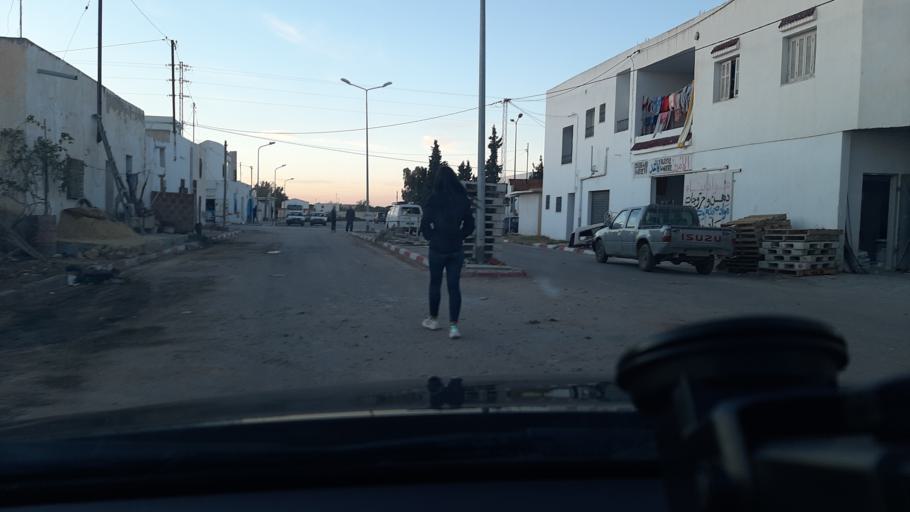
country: TN
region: Al Mahdiyah
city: Shurban
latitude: 34.9617
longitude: 10.3646
